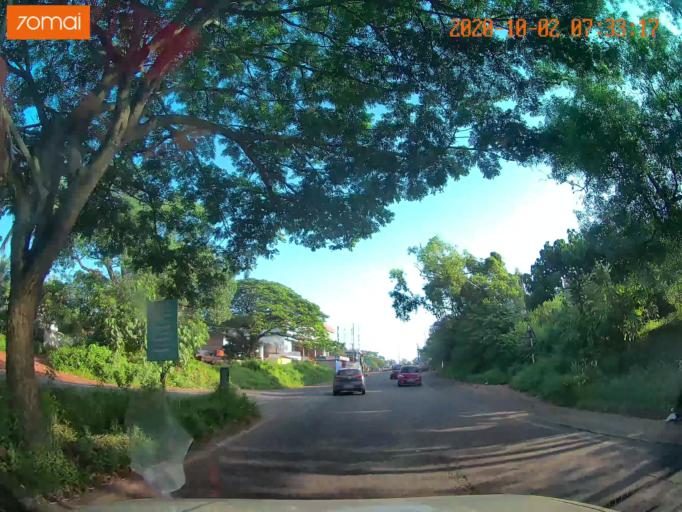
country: IN
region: Kerala
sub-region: Malappuram
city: Pariyapuram
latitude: 11.0578
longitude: 75.9354
